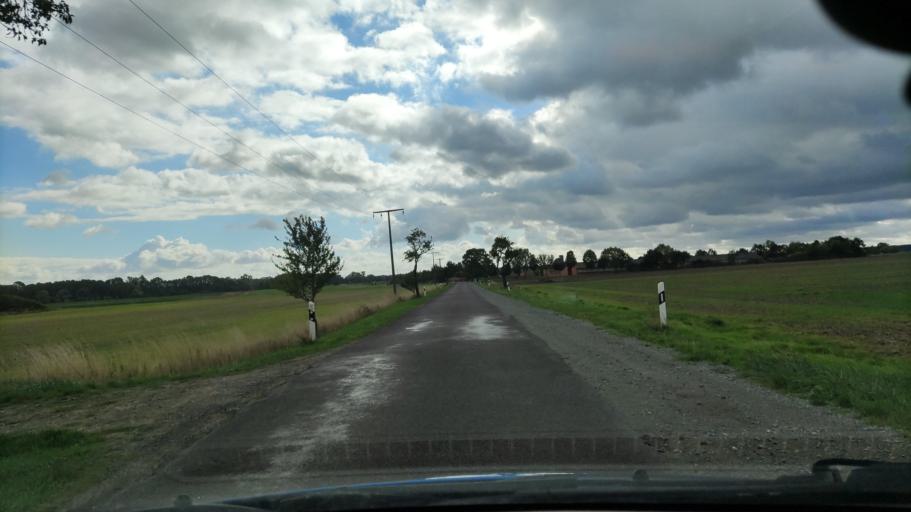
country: DE
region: Saxony-Anhalt
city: Pretzier
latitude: 52.8334
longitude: 11.3480
